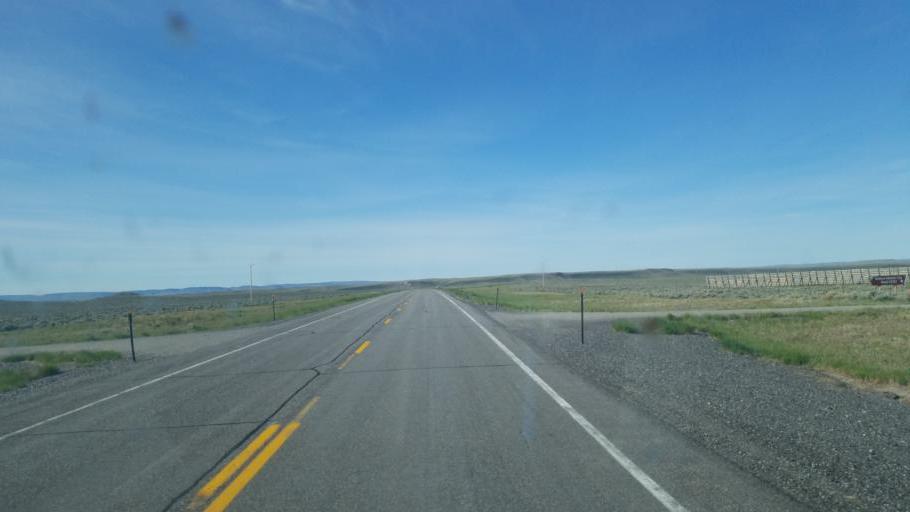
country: US
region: Wyoming
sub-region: Fremont County
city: Riverton
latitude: 42.6400
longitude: -108.1936
